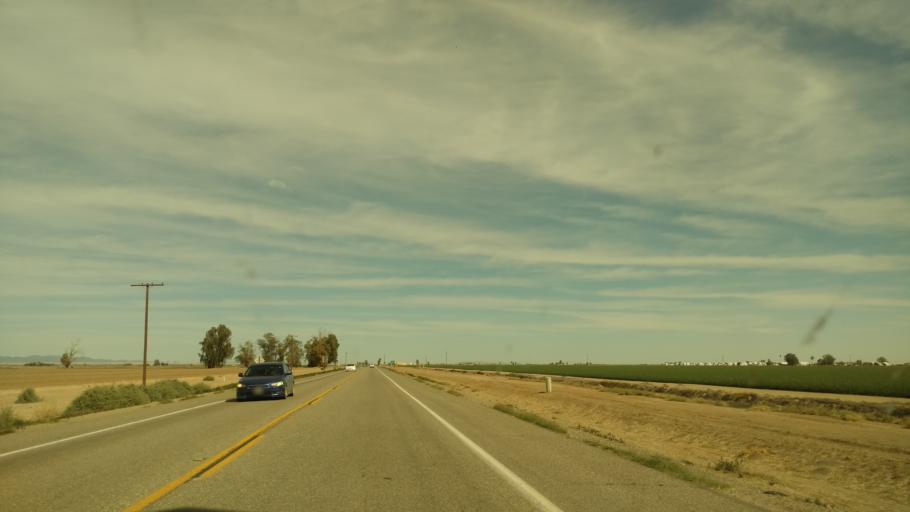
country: US
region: California
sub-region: Imperial County
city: Brawley
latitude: 32.9746
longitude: -115.4552
